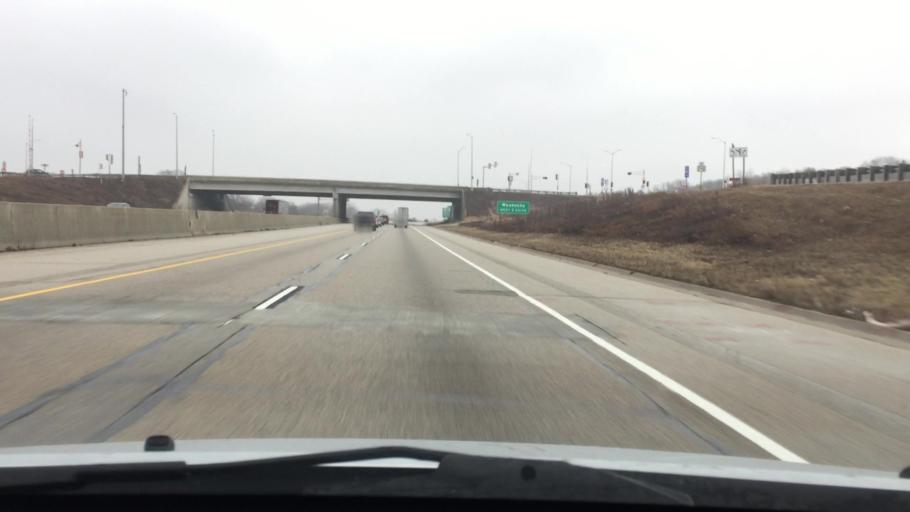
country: US
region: Wisconsin
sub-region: Waukesha County
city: Pewaukee
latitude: 43.0506
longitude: -88.3056
